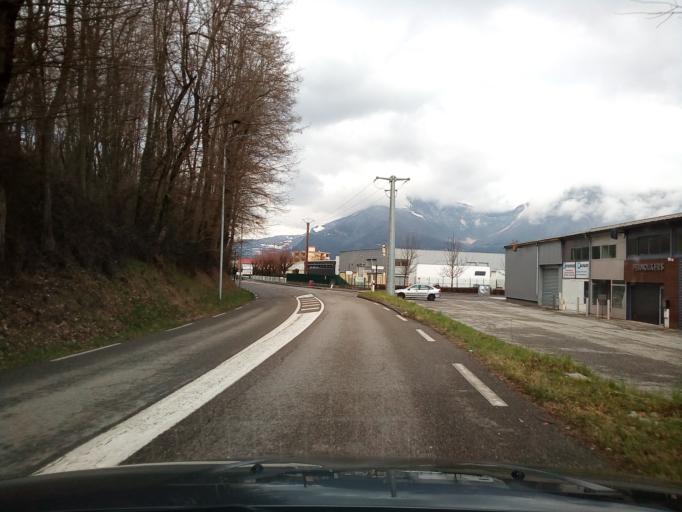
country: FR
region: Rhone-Alpes
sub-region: Departement de la Savoie
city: Saint-Baldoph
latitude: 45.5431
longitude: 5.9586
